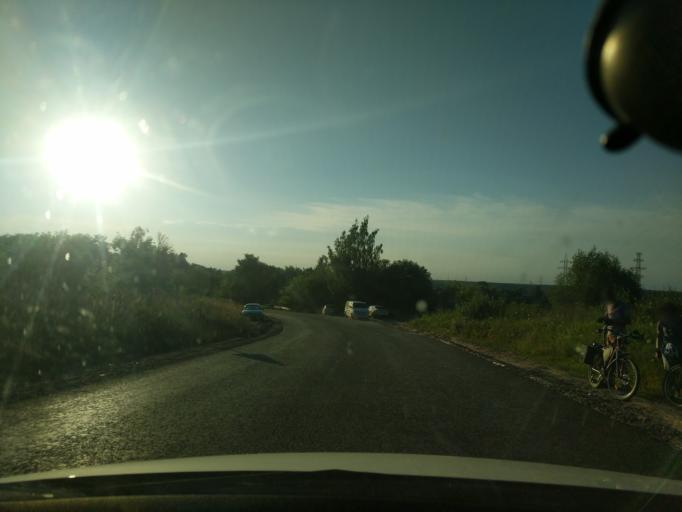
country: RU
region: Moskovskaya
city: Pushchino
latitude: 54.8373
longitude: 37.5938
